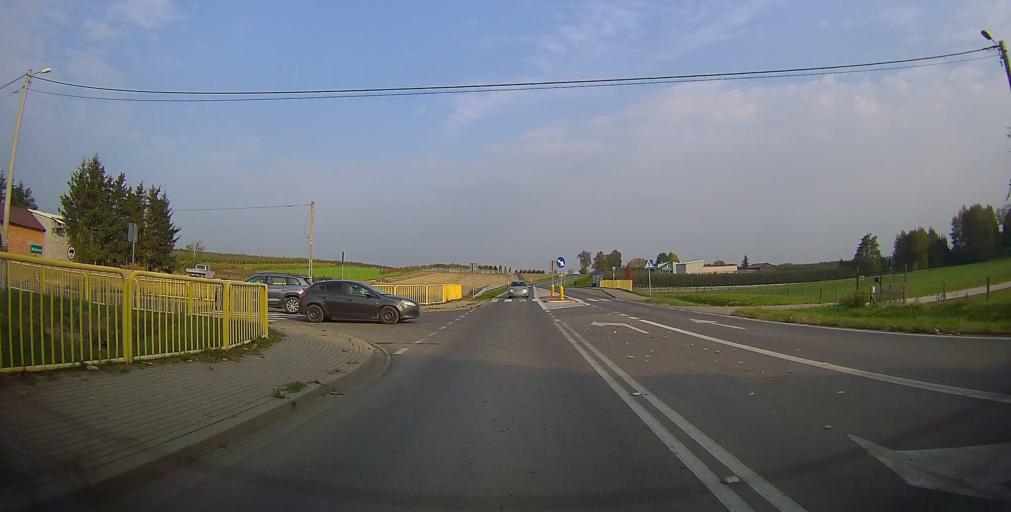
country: PL
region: Masovian Voivodeship
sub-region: Powiat grojecki
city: Mogielnica
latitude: 51.7236
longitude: 20.7470
